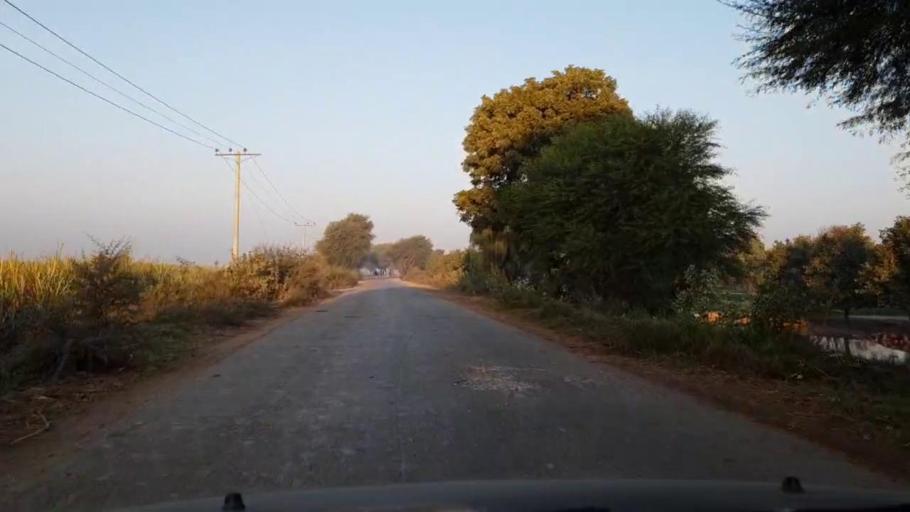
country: PK
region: Sindh
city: Chambar
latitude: 25.2622
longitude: 68.6554
